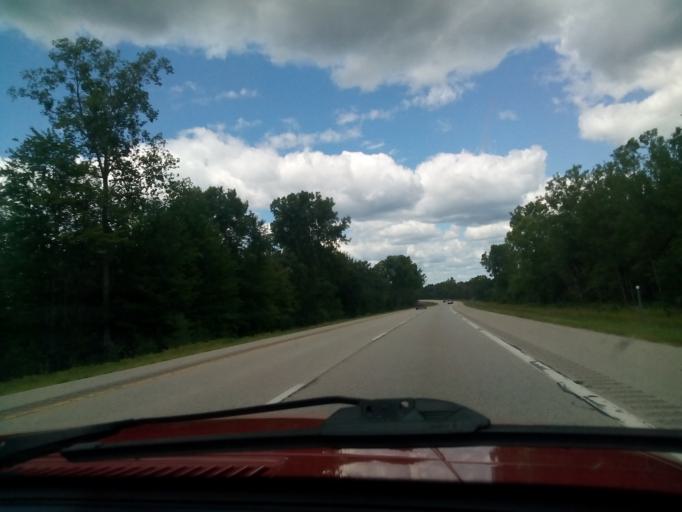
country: US
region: Michigan
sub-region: Ogemaw County
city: Skidway Lake
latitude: 44.0686
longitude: -84.0892
